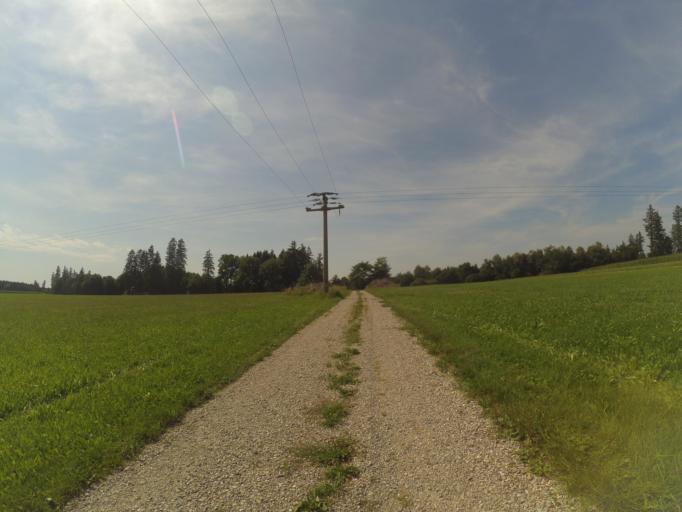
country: DE
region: Bavaria
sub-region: Swabia
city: Unteregg
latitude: 47.9585
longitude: 10.4508
